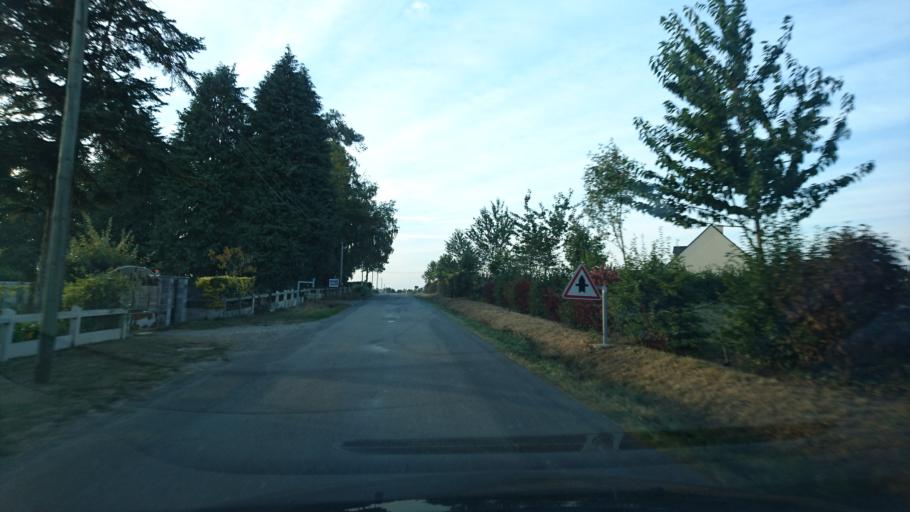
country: FR
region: Brittany
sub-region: Departement d'Ille-et-Vilaine
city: Sixt-sur-Aff
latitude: 47.7619
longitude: -2.0653
